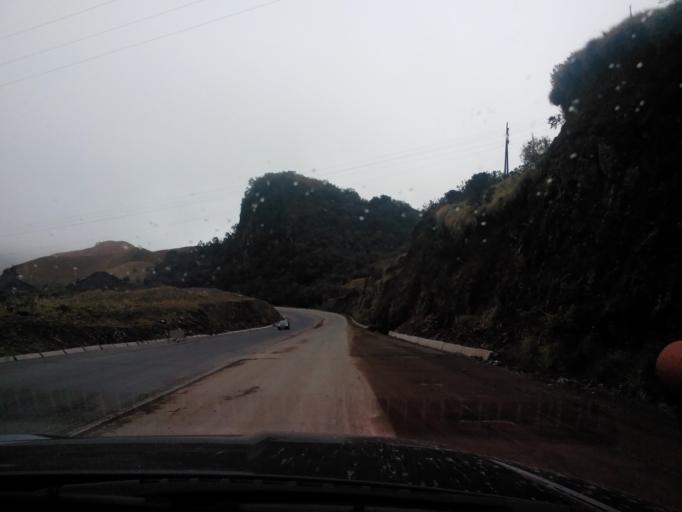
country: EC
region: Pichincha
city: Sangolqui
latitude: -0.3456
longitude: -78.1978
